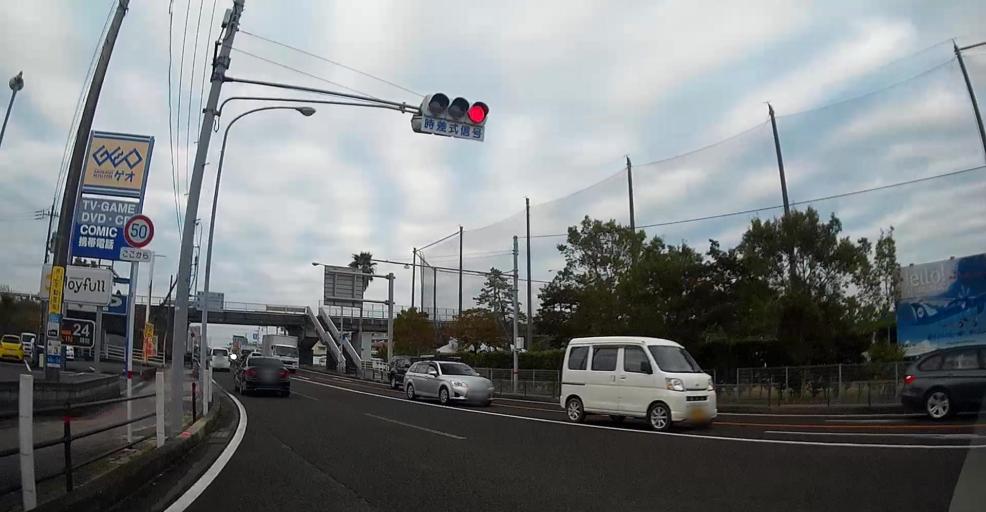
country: JP
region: Kumamoto
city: Hondo
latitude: 32.4468
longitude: 130.2010
